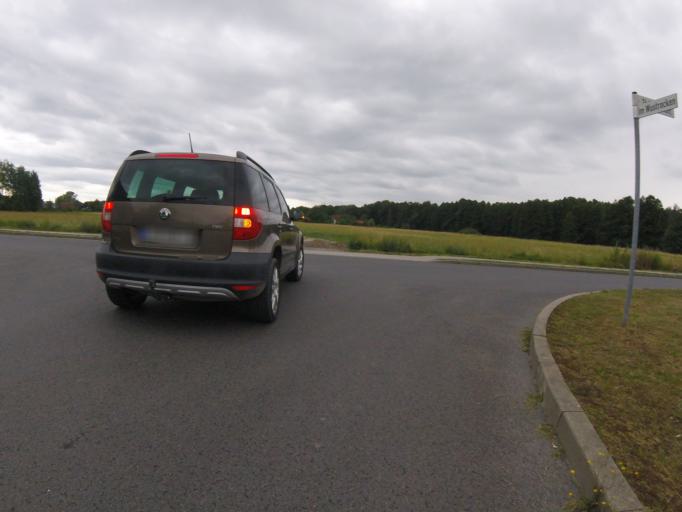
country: DE
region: Brandenburg
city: Bestensee
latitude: 52.2322
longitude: 13.6362
